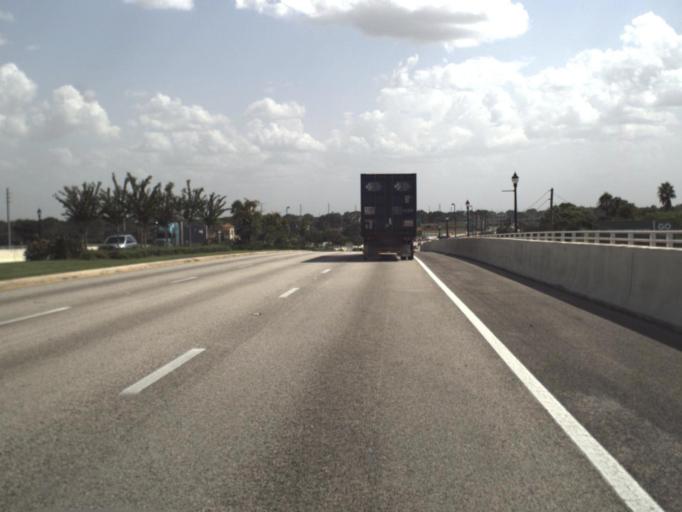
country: US
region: Florida
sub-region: Polk County
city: Lake Wales
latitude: 27.9046
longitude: -81.6009
